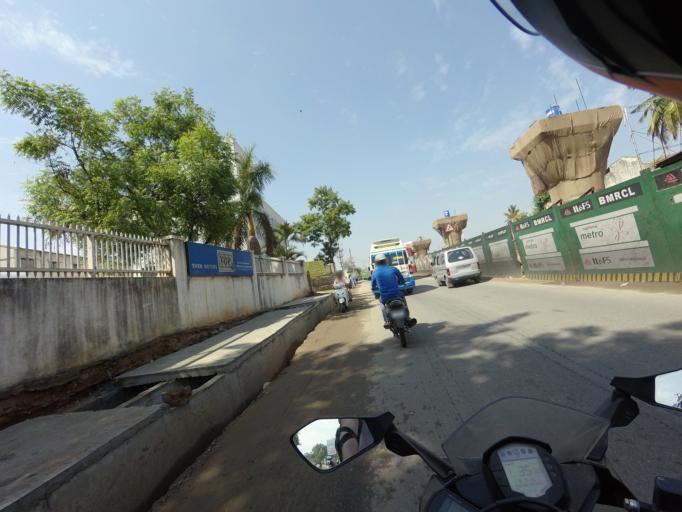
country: IN
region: Karnataka
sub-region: Bangalore Urban
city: Bangalore
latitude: 12.9309
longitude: 77.5063
